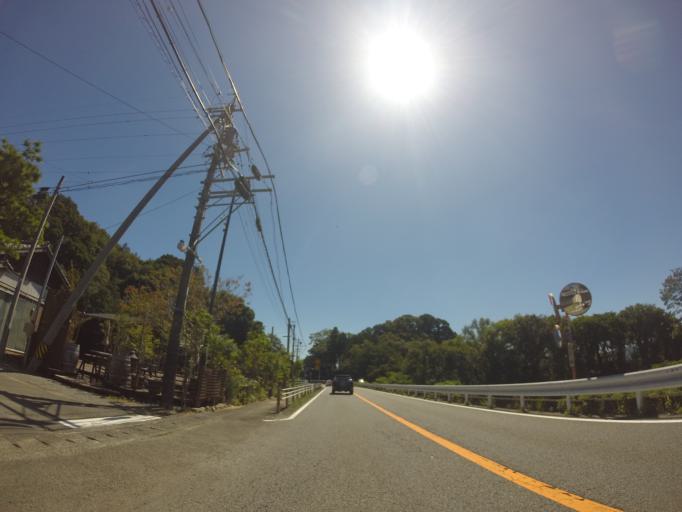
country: JP
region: Shizuoka
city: Kanaya
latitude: 34.8452
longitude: 138.1445
